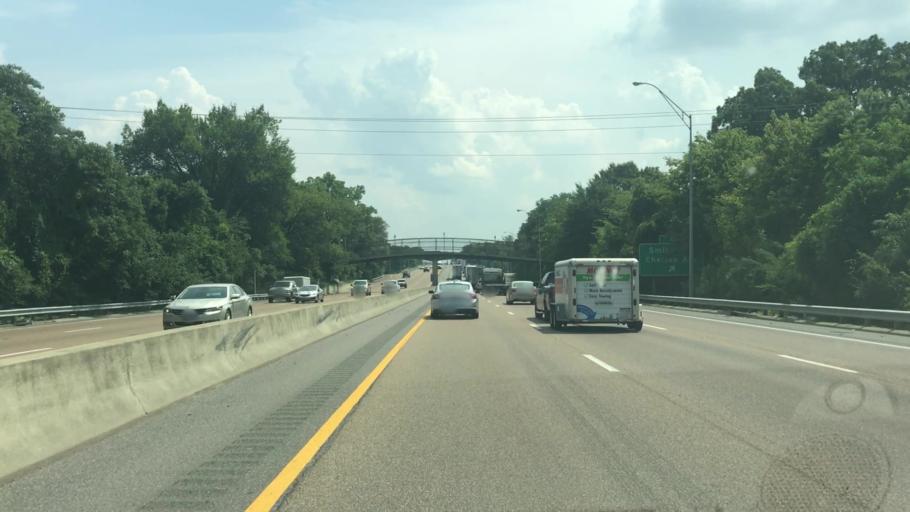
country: US
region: Tennessee
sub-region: Shelby County
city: Memphis
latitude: 35.1791
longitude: -90.0181
